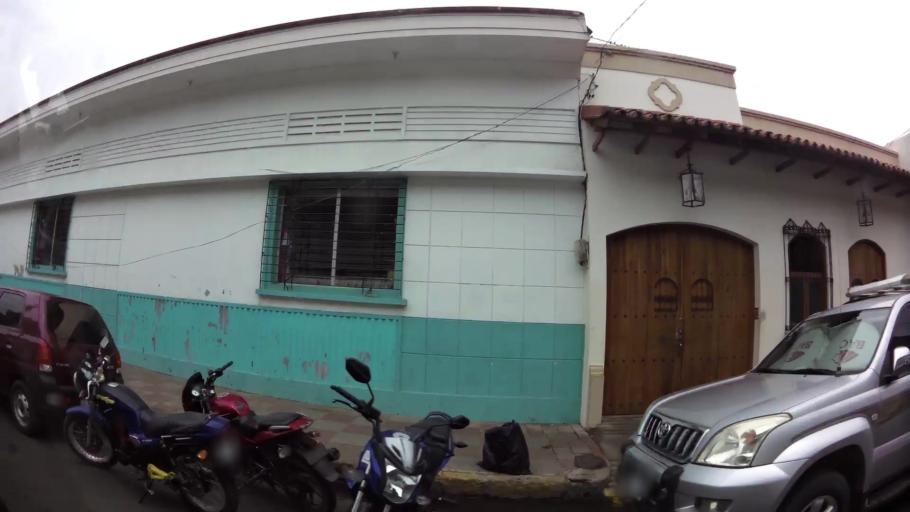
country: NI
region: Leon
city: Leon
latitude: 12.4362
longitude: -86.8756
